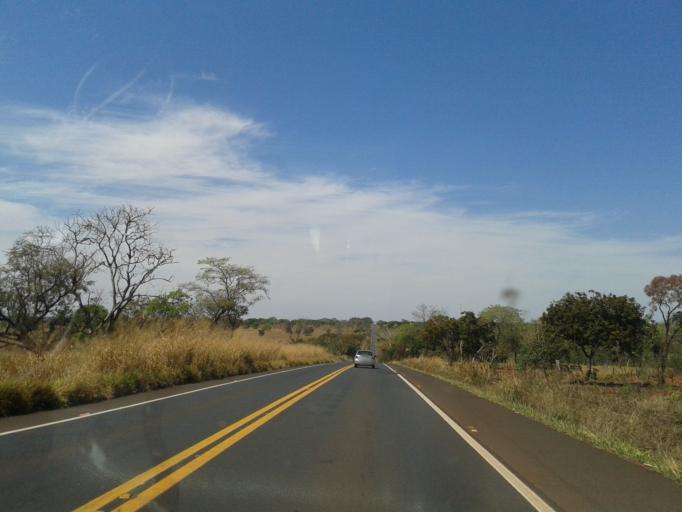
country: BR
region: Minas Gerais
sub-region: Santa Vitoria
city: Santa Vitoria
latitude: -18.9226
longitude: -49.8624
